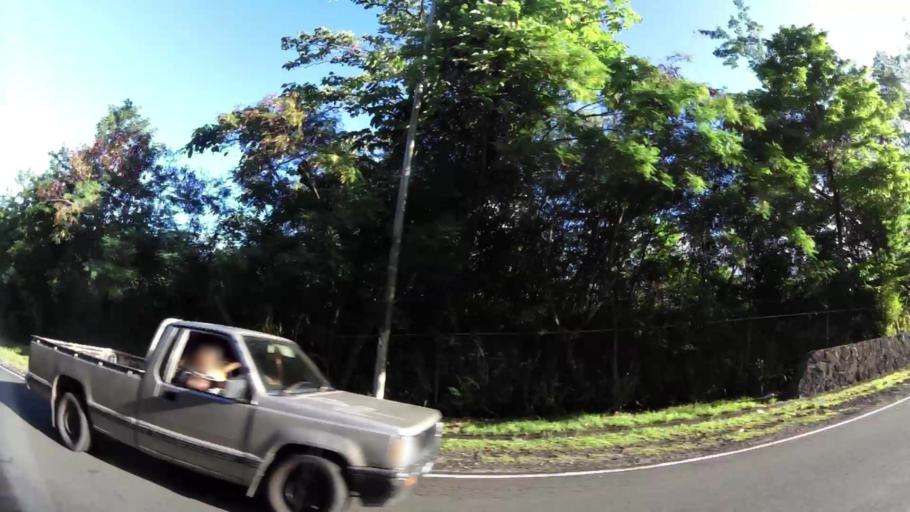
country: LC
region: Castries Quarter
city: Castries
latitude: 14.0044
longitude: -61.0047
